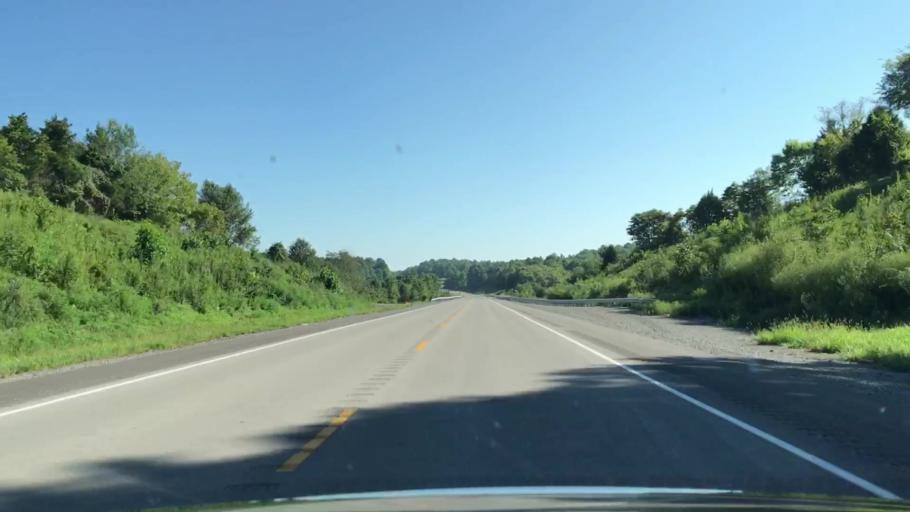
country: US
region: Kentucky
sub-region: Cumberland County
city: Burkesville
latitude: 36.6445
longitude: -85.3824
